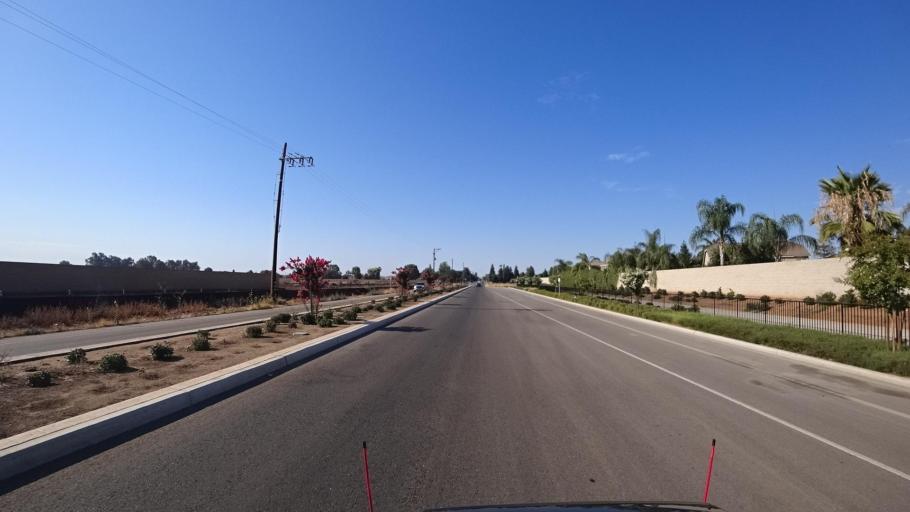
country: US
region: California
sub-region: Fresno County
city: Tarpey Village
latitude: 36.7770
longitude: -119.6641
